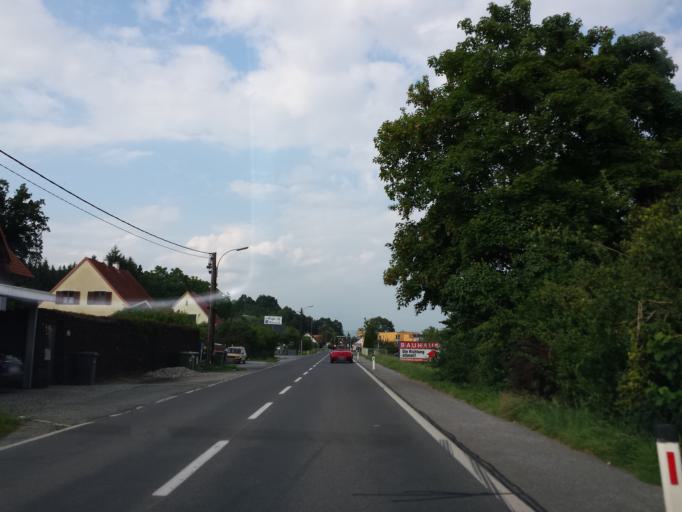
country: AT
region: Styria
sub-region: Politischer Bezirk Graz-Umgebung
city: Seiersberg
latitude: 47.0028
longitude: 15.3918
